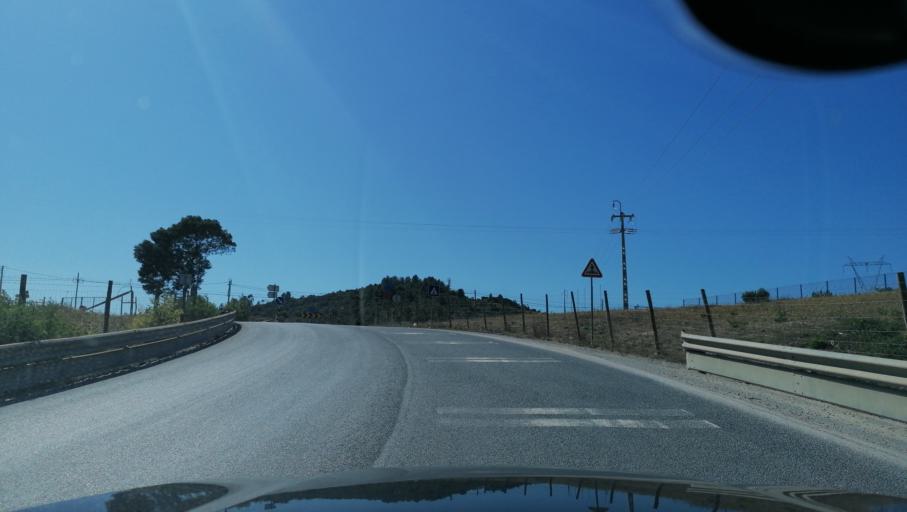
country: PT
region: Lisbon
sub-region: Alenquer
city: Alenquer
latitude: 39.0669
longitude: -9.0044
